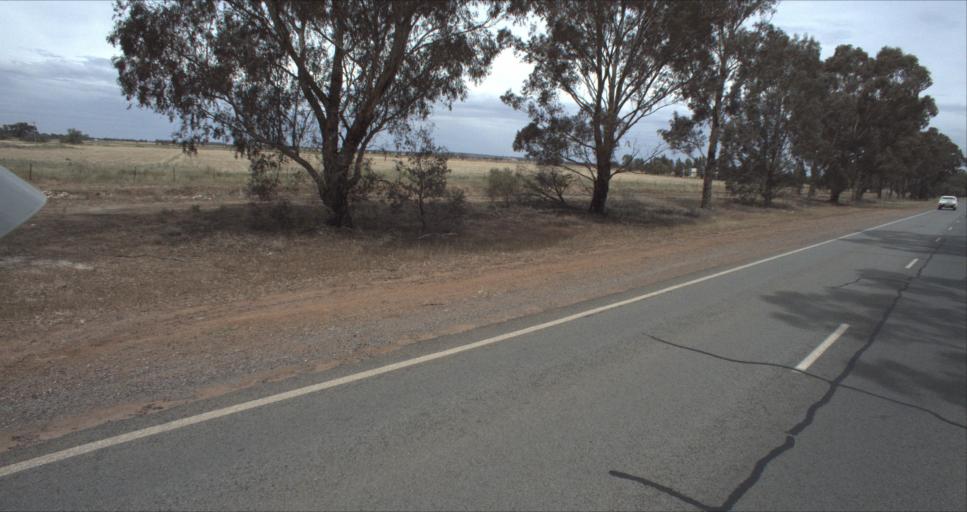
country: AU
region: New South Wales
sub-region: Leeton
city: Leeton
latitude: -34.5123
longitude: 146.4194
